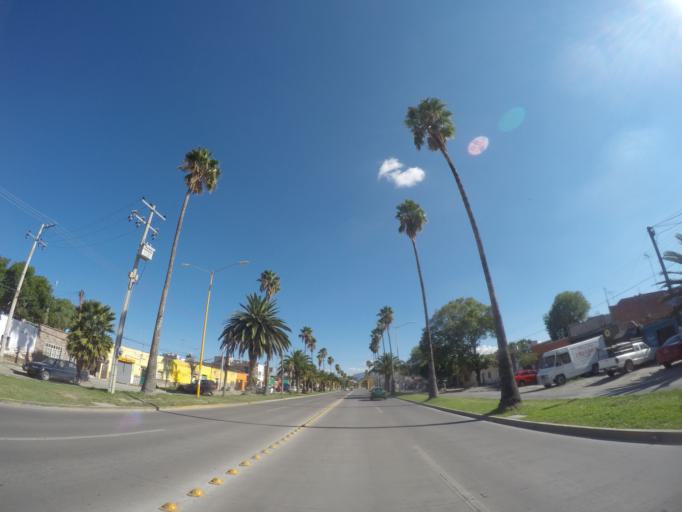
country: MX
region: San Luis Potosi
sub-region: San Luis Potosi
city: San Luis Potosi
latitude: 22.1661
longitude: -100.9723
